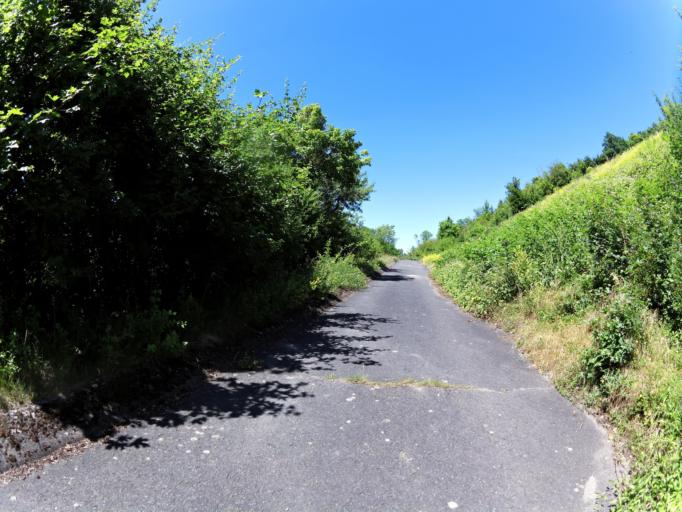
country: DE
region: Bavaria
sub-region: Regierungsbezirk Unterfranken
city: Frickenhausen
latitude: 49.6721
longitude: 10.0798
